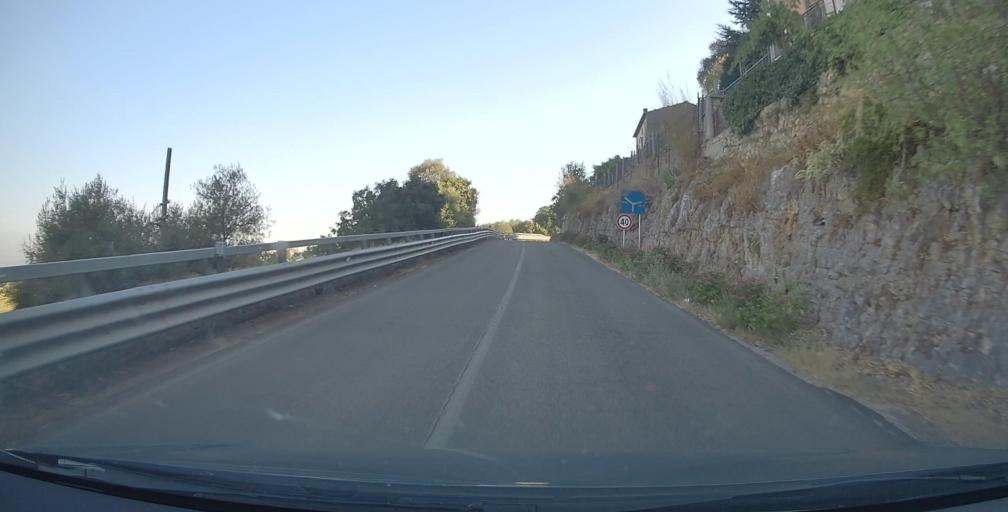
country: IT
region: Umbria
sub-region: Provincia di Terni
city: Calvi dell'Umbria
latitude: 42.4024
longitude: 12.5651
